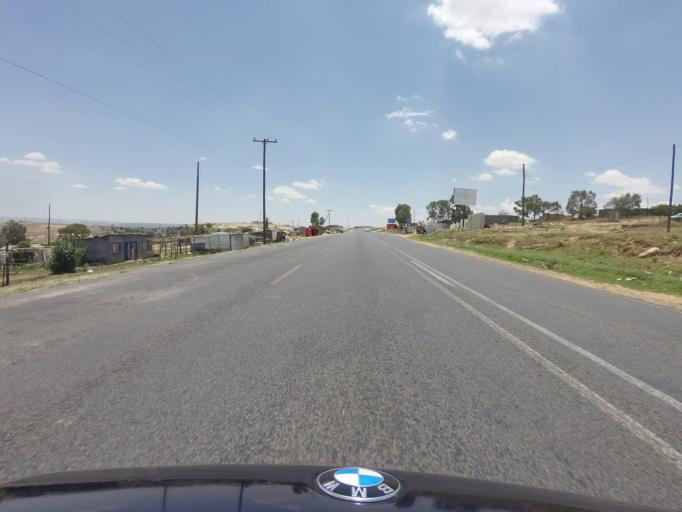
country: LS
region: Berea
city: Teyateyaneng
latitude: -29.1532
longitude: 27.6809
